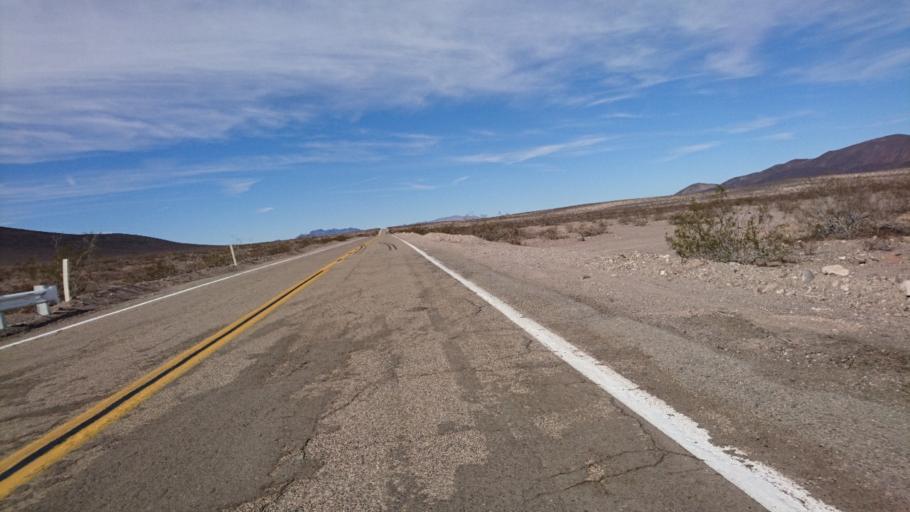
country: US
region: California
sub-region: San Bernardino County
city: Twentynine Palms
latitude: 34.6951
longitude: -116.0536
